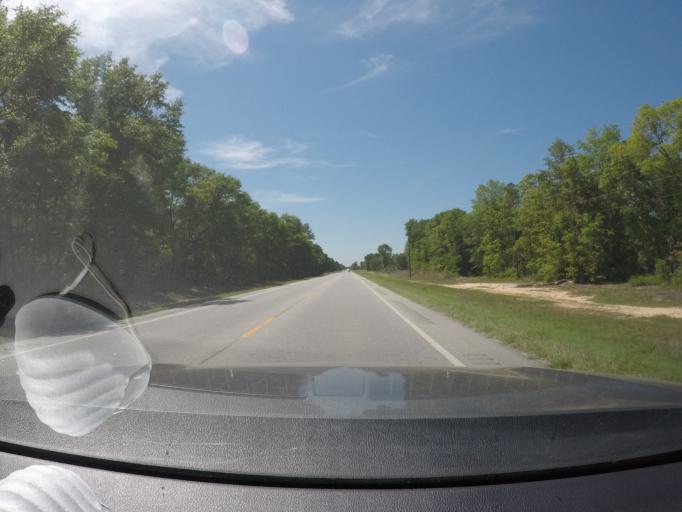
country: US
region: Georgia
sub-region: Bryan County
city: Pembroke
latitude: 32.1452
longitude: -81.7525
